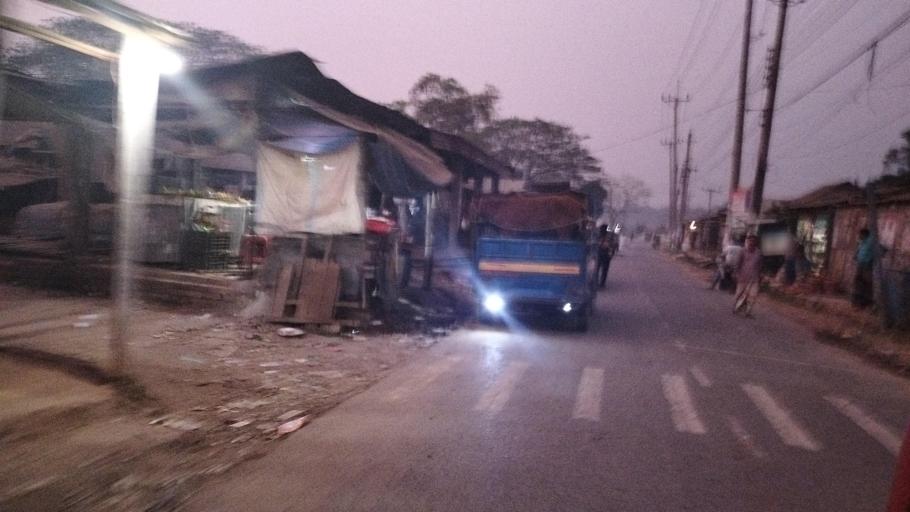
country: BD
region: Dhaka
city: Sakhipur
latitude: 24.3910
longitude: 90.3315
